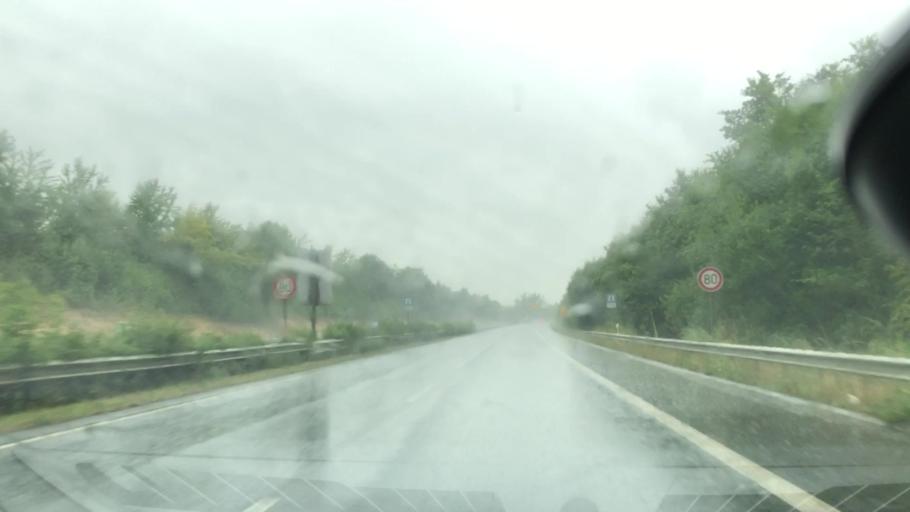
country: DE
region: North Rhine-Westphalia
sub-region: Regierungsbezirk Detmold
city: Minden
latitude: 52.2727
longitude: 8.9072
